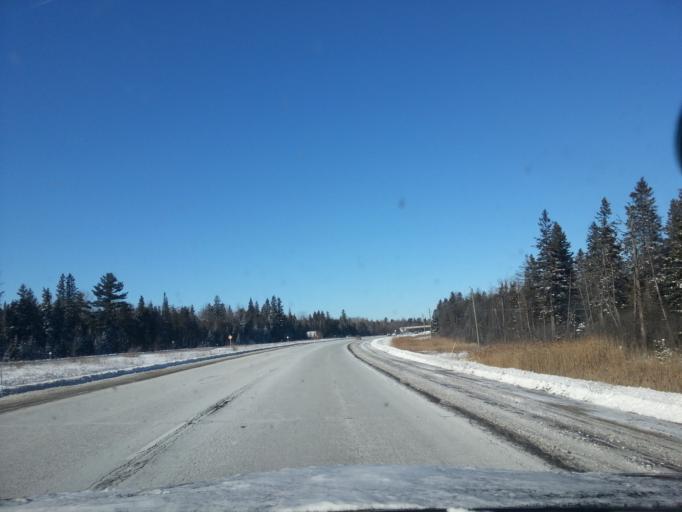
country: CA
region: Ontario
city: Bells Corners
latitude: 45.2739
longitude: -75.9895
